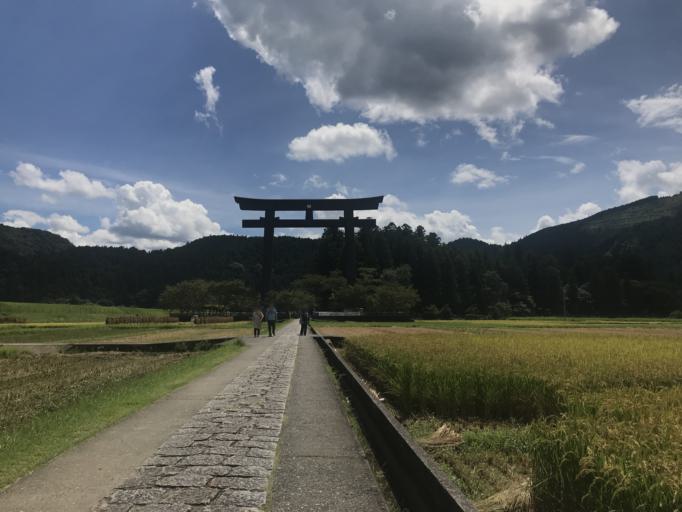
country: JP
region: Wakayama
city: Shingu
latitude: 33.8372
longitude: 135.7756
